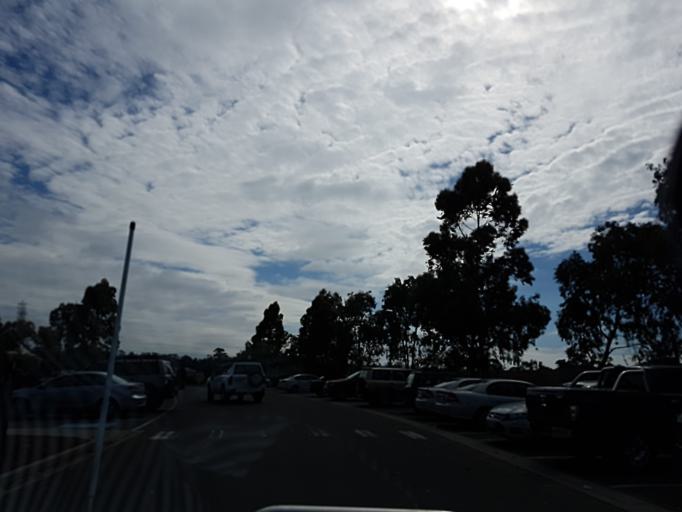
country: AU
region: Victoria
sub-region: Cardinia
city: Bunyip
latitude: -38.0856
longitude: 145.7752
